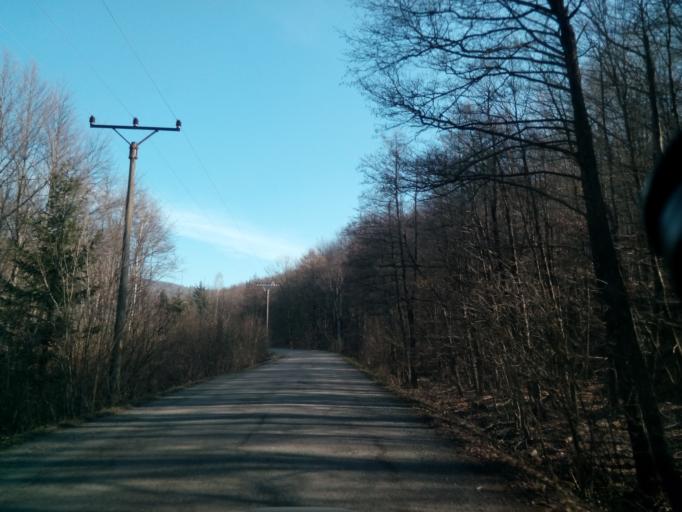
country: SK
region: Presovsky
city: Snina
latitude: 48.8733
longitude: 22.2068
